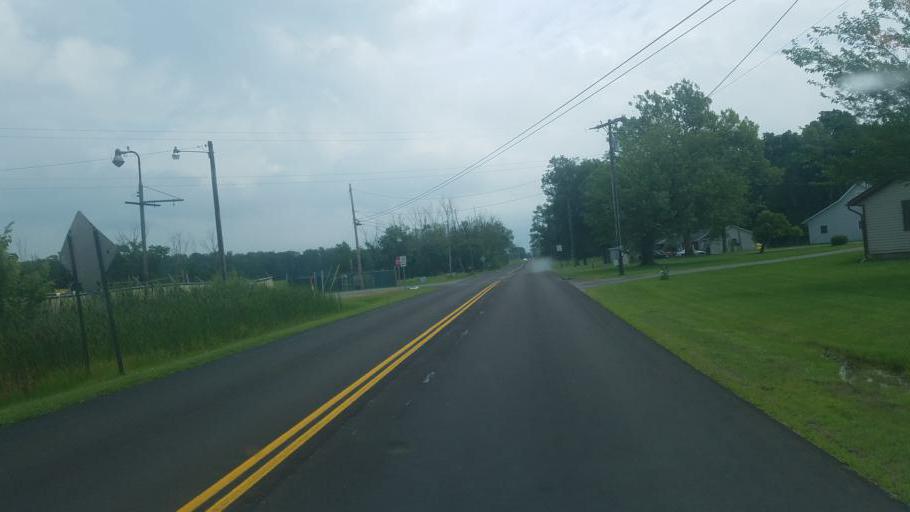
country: US
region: Ohio
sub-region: Logan County
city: Russells Point
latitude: 40.4705
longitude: -83.8414
